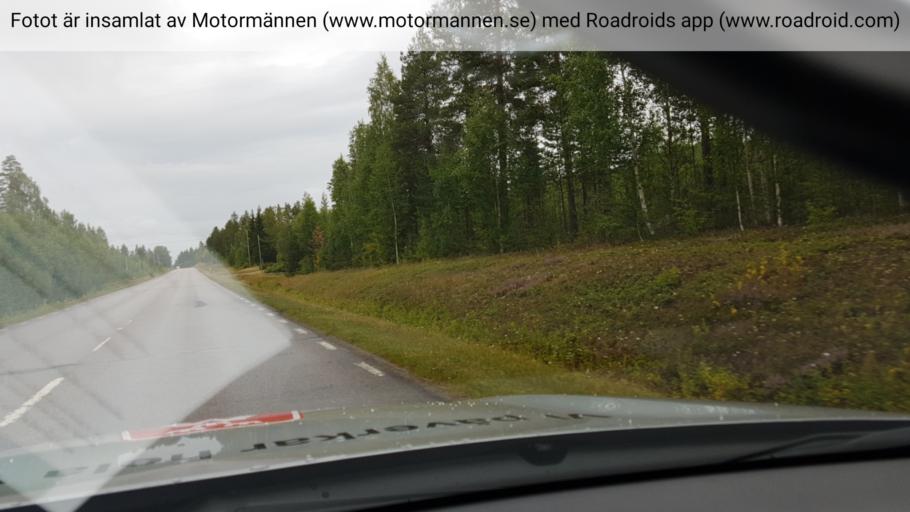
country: SE
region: Norrbotten
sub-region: Alvsbyns Kommun
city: AElvsbyn
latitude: 66.1033
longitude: 20.9375
